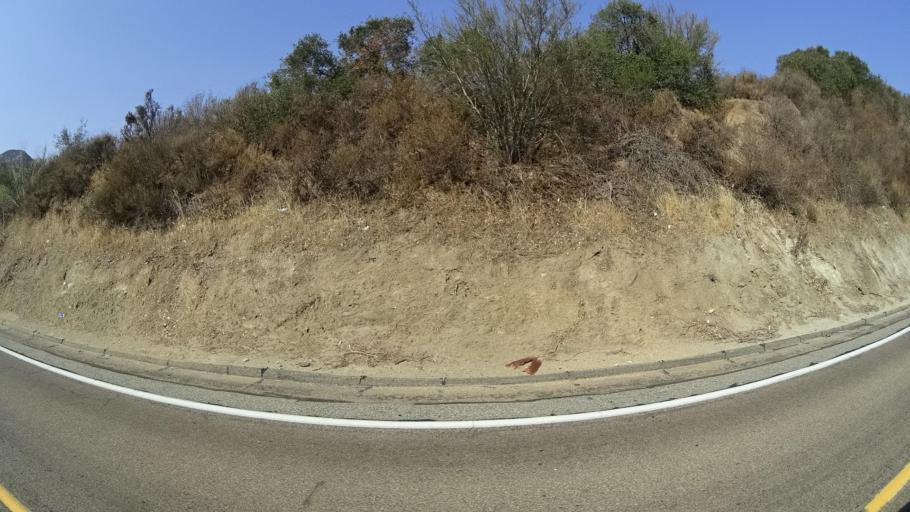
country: US
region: California
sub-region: San Diego County
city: Hidden Meadows
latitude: 33.2293
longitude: -117.1440
